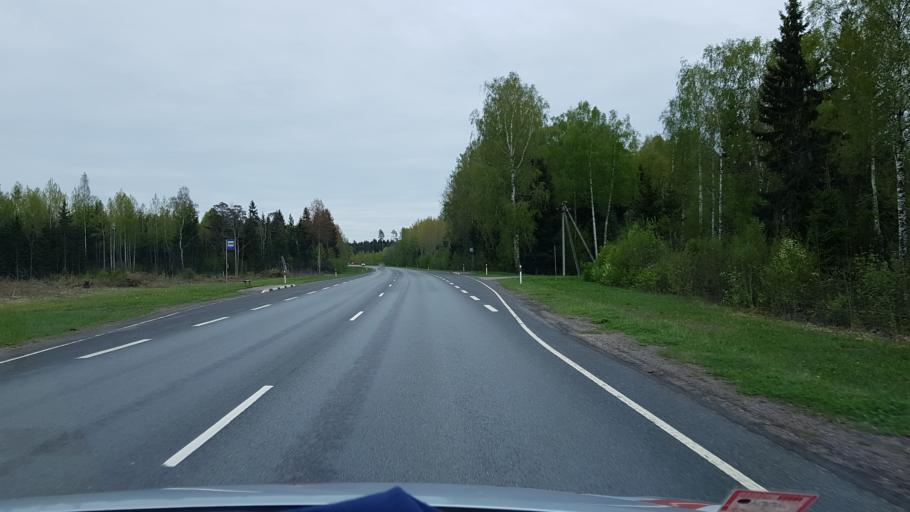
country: EE
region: Harju
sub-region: Nissi vald
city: Turba
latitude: 58.9752
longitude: 24.0598
